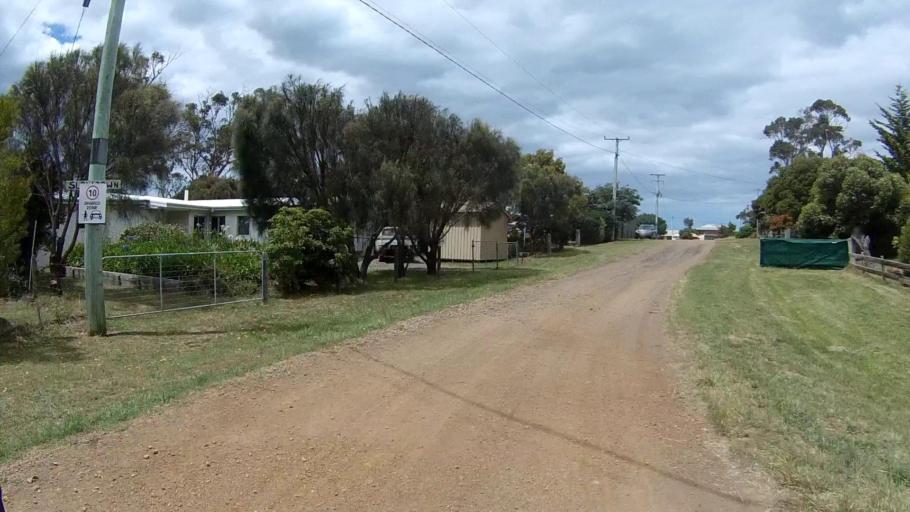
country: AU
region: Tasmania
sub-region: Sorell
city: Sorell
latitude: -42.6619
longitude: 147.9527
